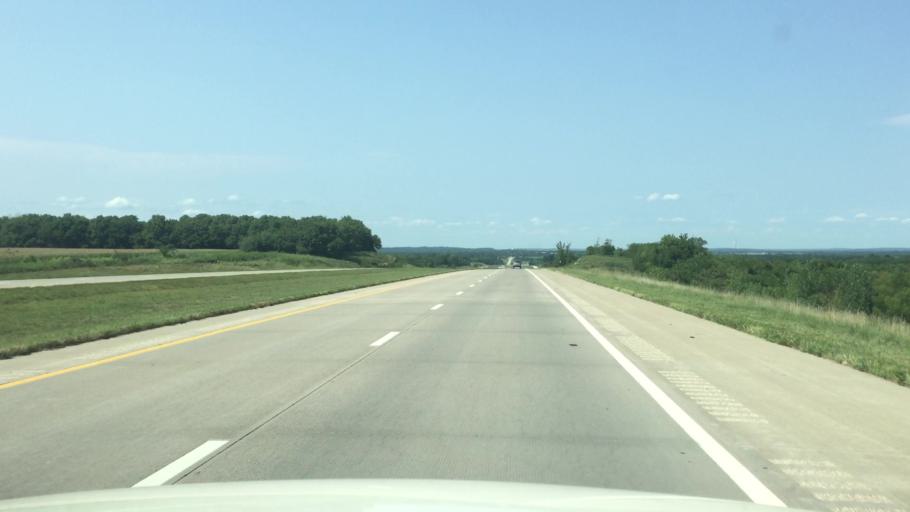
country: US
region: Kansas
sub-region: Linn County
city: Pleasanton
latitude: 38.1117
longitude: -94.7133
